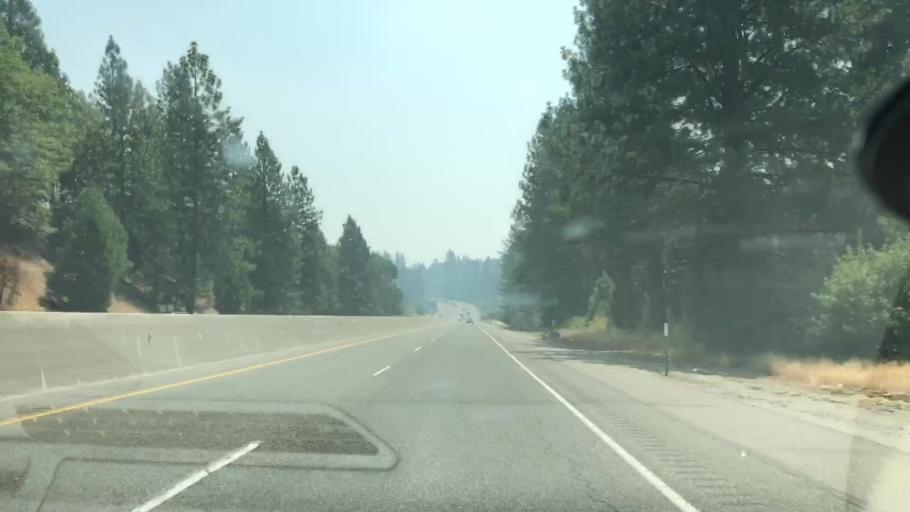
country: US
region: California
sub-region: El Dorado County
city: Camino
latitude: 38.7378
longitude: -120.6898
